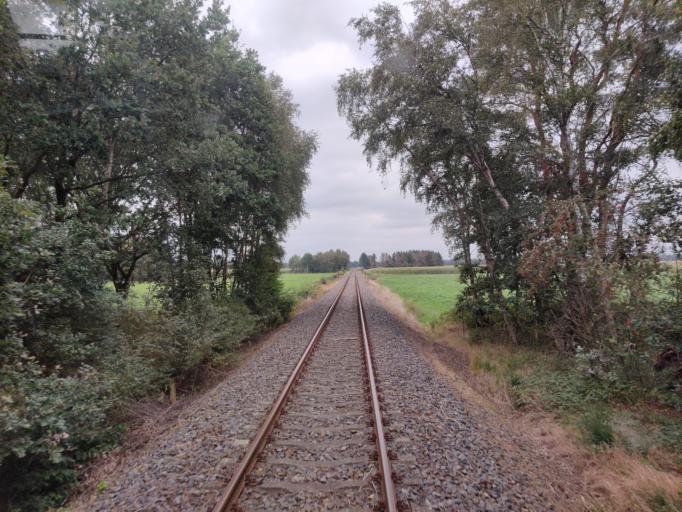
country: DE
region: Lower Saxony
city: Worpswede
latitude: 53.2801
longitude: 8.9655
